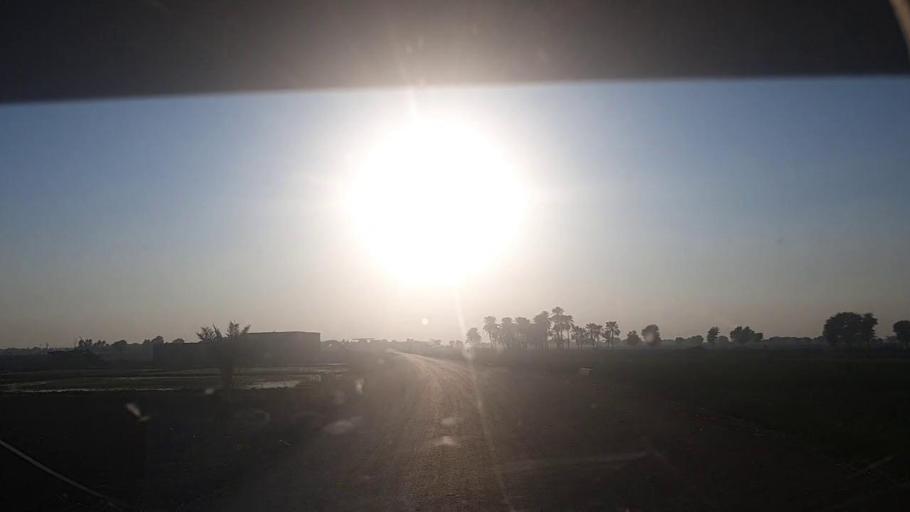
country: PK
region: Sindh
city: Hingorja
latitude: 27.2212
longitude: 68.4068
